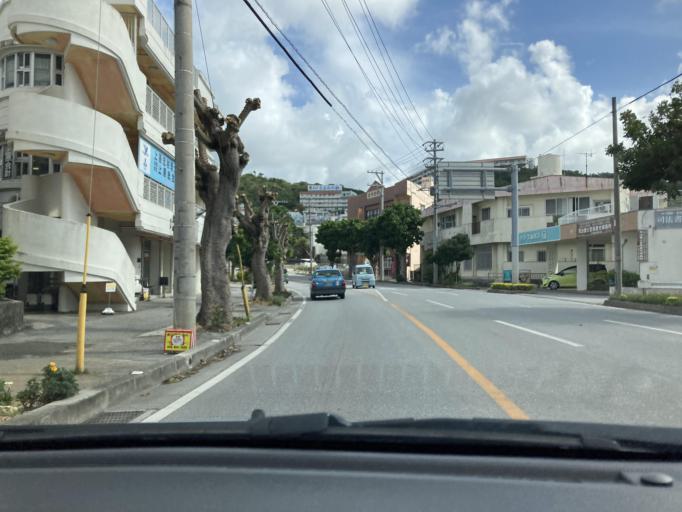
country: JP
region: Okinawa
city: Tomigusuku
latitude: 26.1762
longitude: 127.6825
